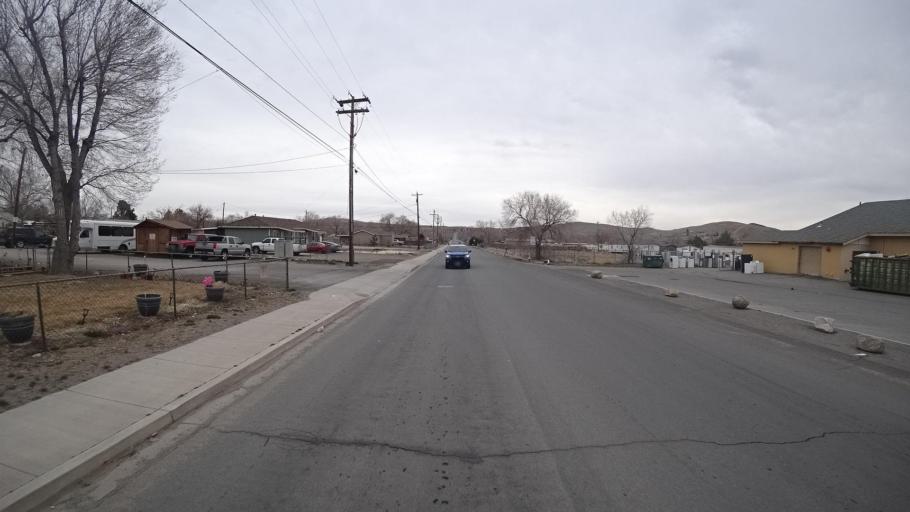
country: US
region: Nevada
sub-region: Washoe County
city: Sun Valley
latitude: 39.5928
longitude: -119.7797
